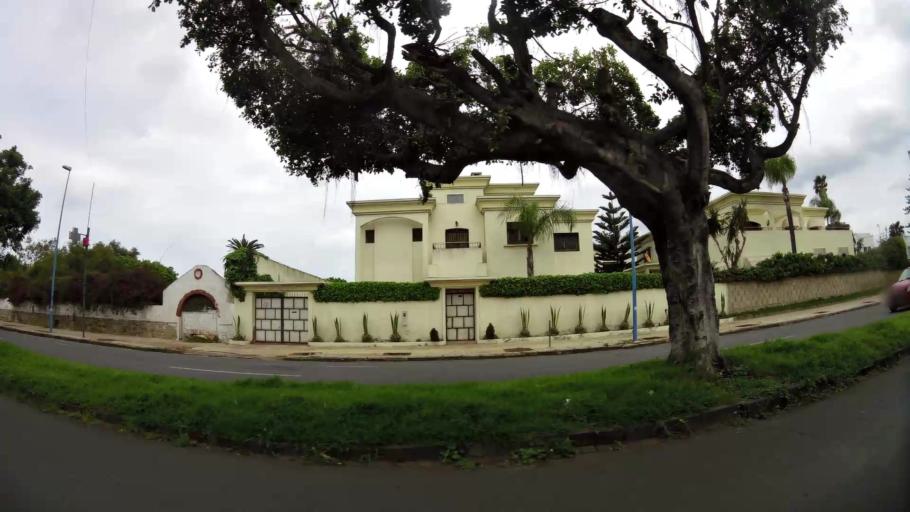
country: MA
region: Grand Casablanca
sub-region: Casablanca
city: Casablanca
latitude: 33.5593
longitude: -7.6383
